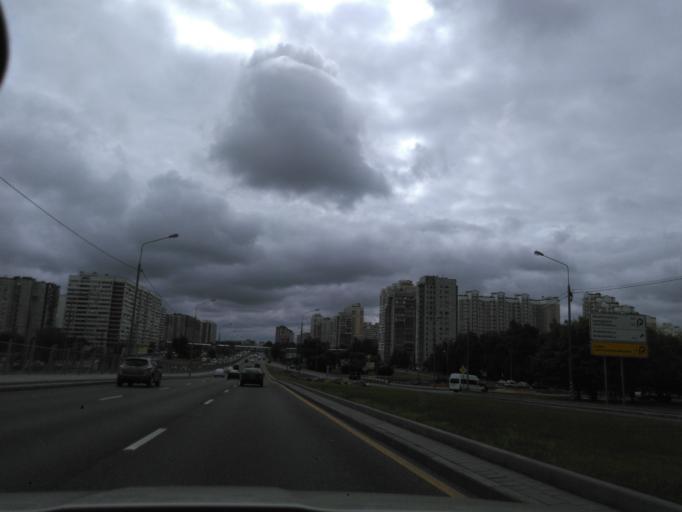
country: RU
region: Moskovskaya
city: Bol'shaya Setun'
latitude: 55.7455
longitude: 37.4205
